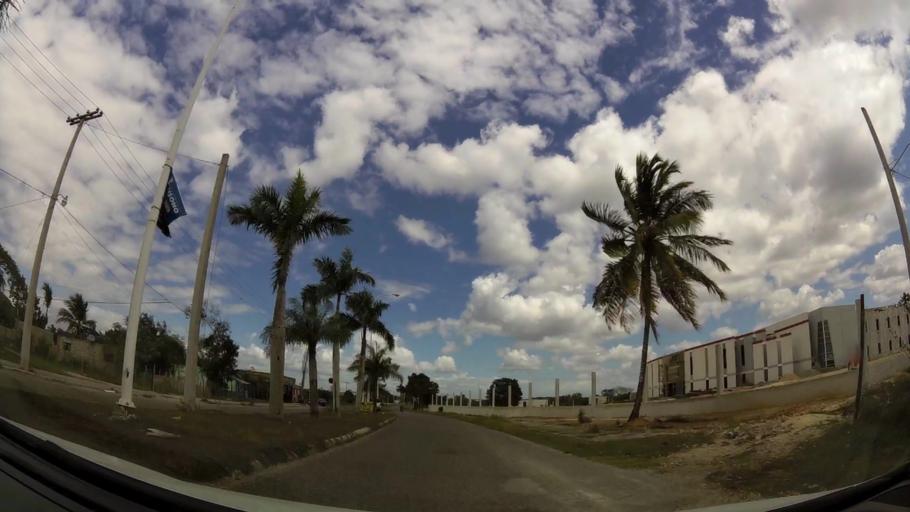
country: DO
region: Santo Domingo
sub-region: Santo Domingo
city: Boca Chica
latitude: 18.4559
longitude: -69.6618
